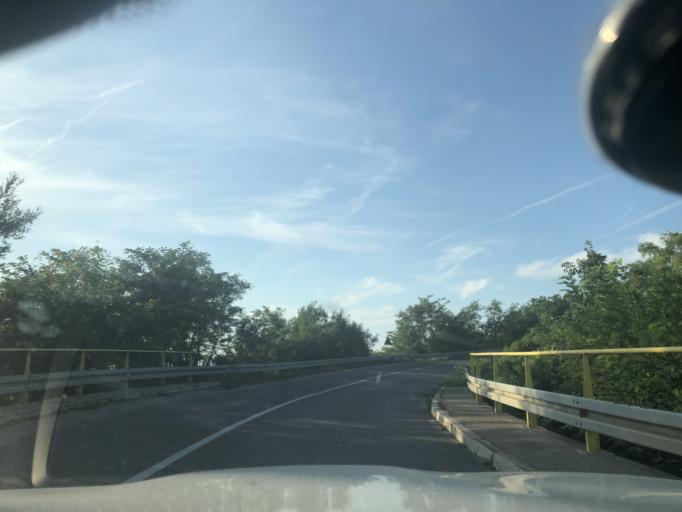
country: RS
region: Central Serbia
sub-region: Nisavski Okrug
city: Aleksinac
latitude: 43.4780
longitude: 21.7723
